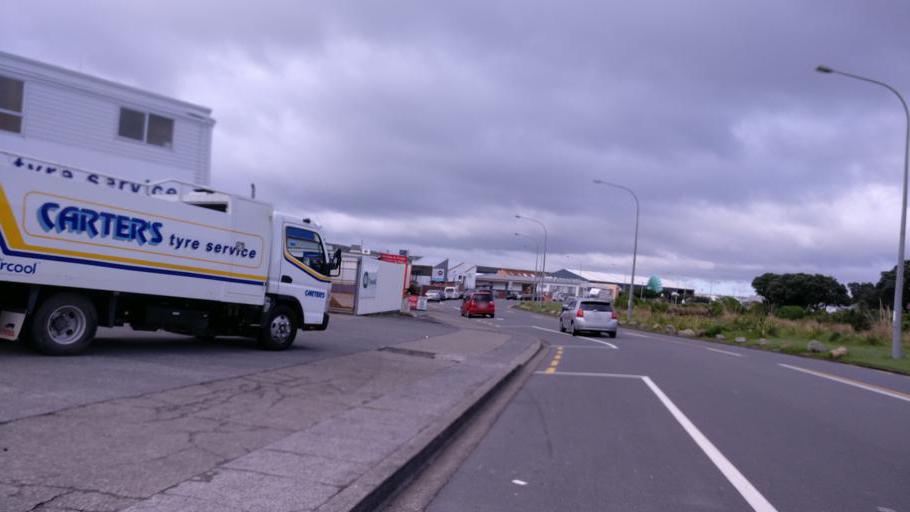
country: NZ
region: Wellington
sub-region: Lower Hutt City
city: Lower Hutt
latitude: -41.2354
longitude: 174.9123
